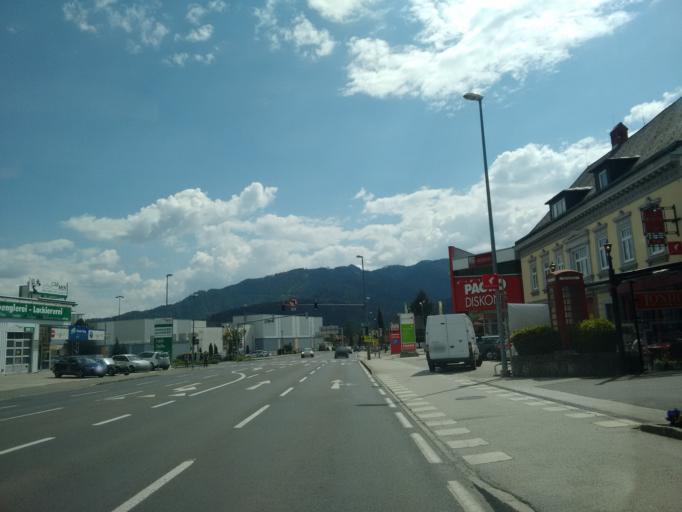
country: AT
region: Styria
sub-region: Politischer Bezirk Bruck-Muerzzuschlag
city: Bruck an der Mur
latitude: 47.4191
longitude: 15.2743
